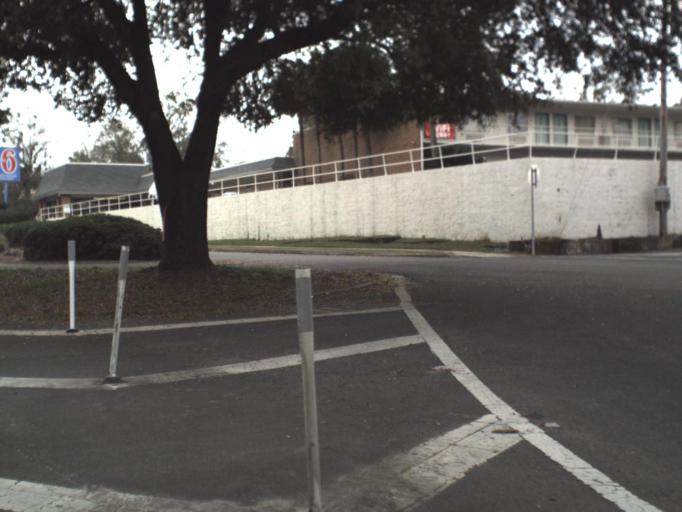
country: US
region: Florida
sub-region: Leon County
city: Tallahassee
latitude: 30.4380
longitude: -84.2679
